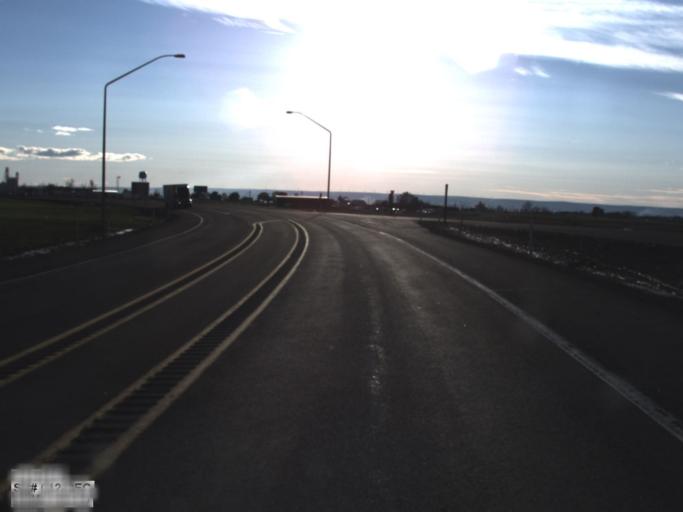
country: US
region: Washington
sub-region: Walla Walla County
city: Walla Walla East
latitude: 46.0999
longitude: -118.2522
